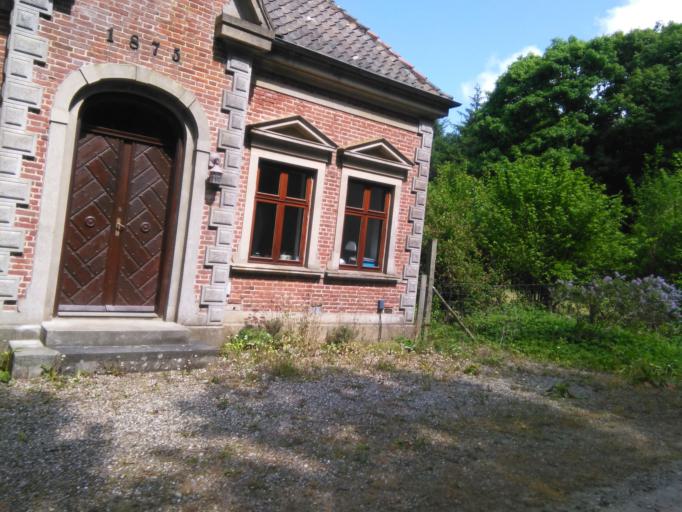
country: DK
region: Central Jutland
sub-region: Favrskov Kommune
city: Hammel
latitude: 56.2664
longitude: 9.9316
